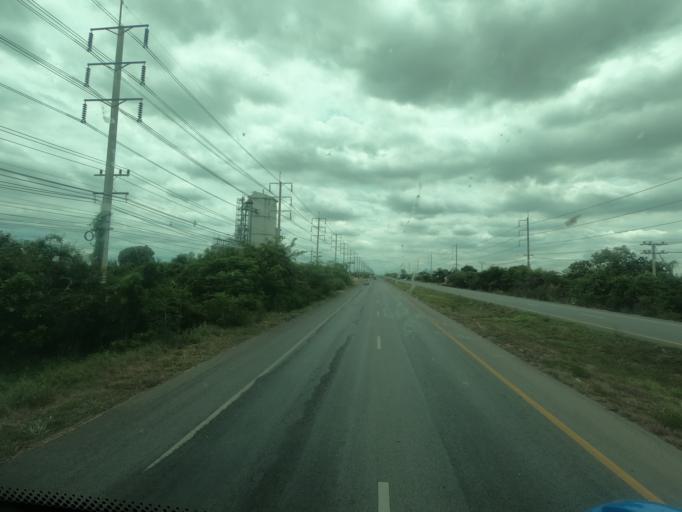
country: TH
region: Nakhon Ratchasima
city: Chok Chai
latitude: 14.7376
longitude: 102.1207
